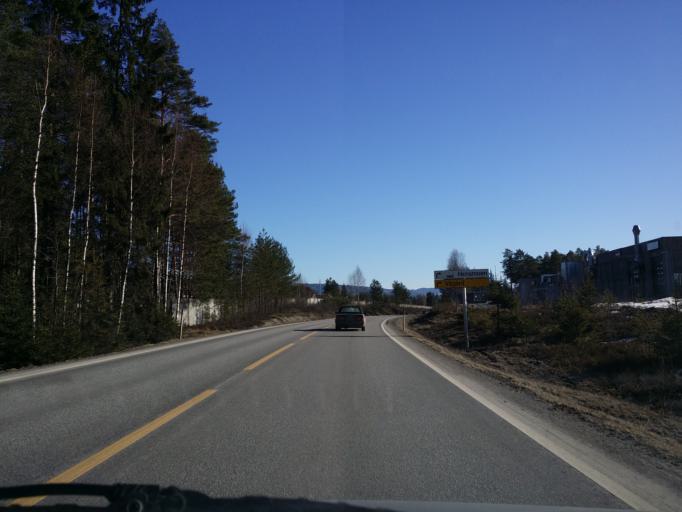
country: NO
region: Buskerud
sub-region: Ringerike
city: Honefoss
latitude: 60.2240
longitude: 10.2547
